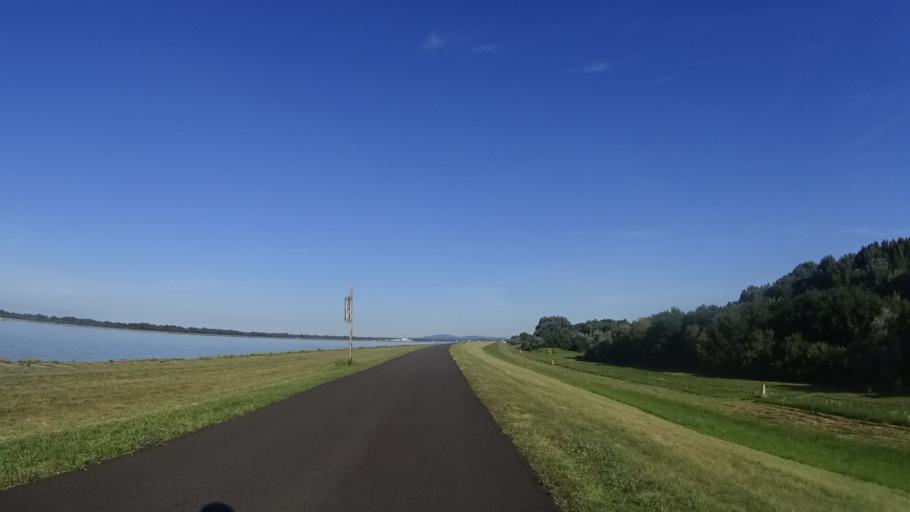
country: SK
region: Trnavsky
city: Samorin
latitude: 48.0259
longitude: 17.2661
